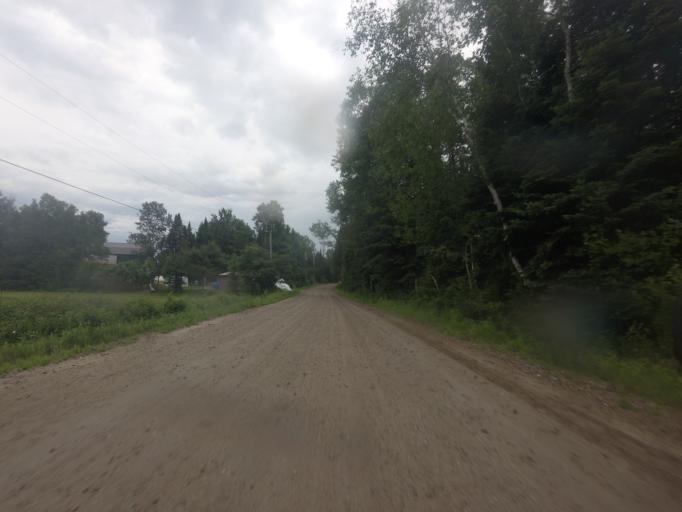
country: CA
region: Quebec
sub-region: Outaouais
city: Maniwaki
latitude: 46.4442
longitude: -75.9351
